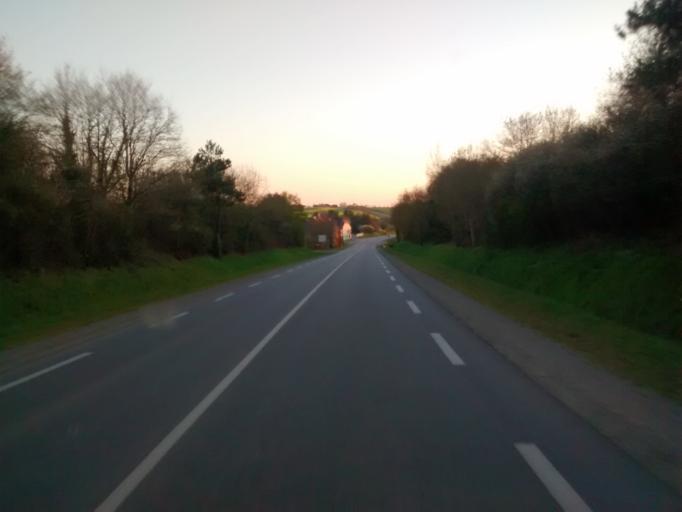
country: FR
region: Brittany
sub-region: Departement du Morbihan
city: Loyat
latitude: 47.9953
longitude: -2.3593
